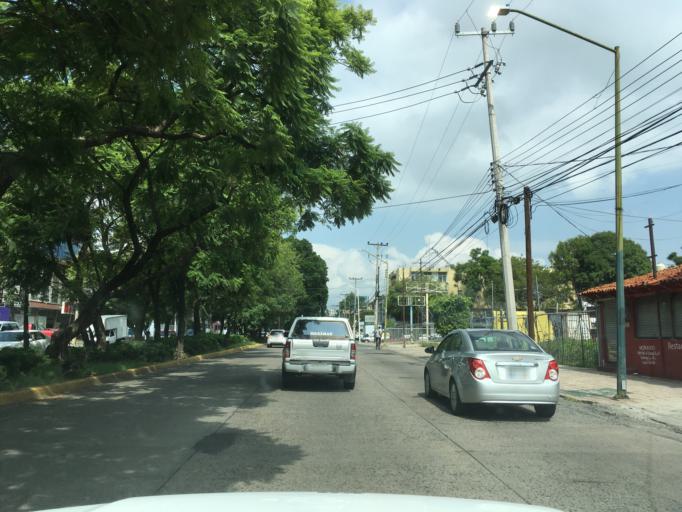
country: MX
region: Jalisco
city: Guadalajara
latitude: 20.6666
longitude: -103.3887
